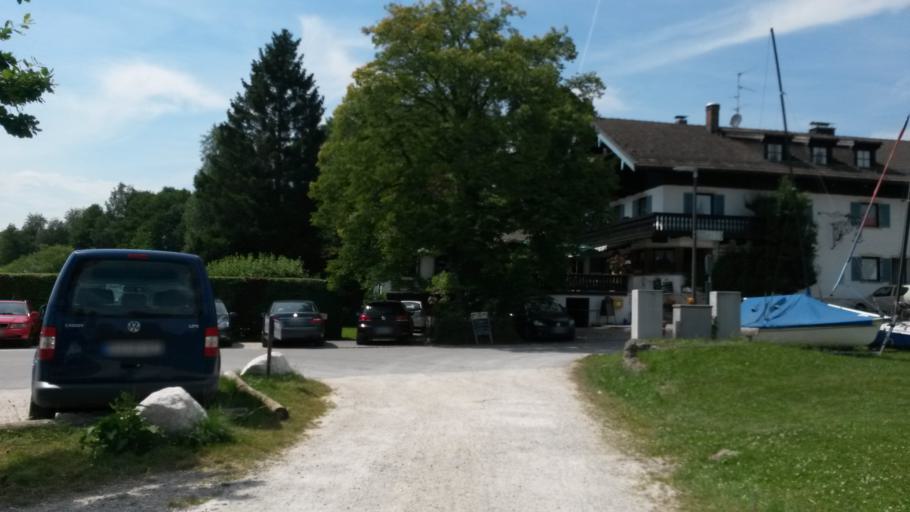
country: DE
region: Bavaria
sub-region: Upper Bavaria
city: Gstadt am Chiemsee
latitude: 47.8832
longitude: 12.3975
